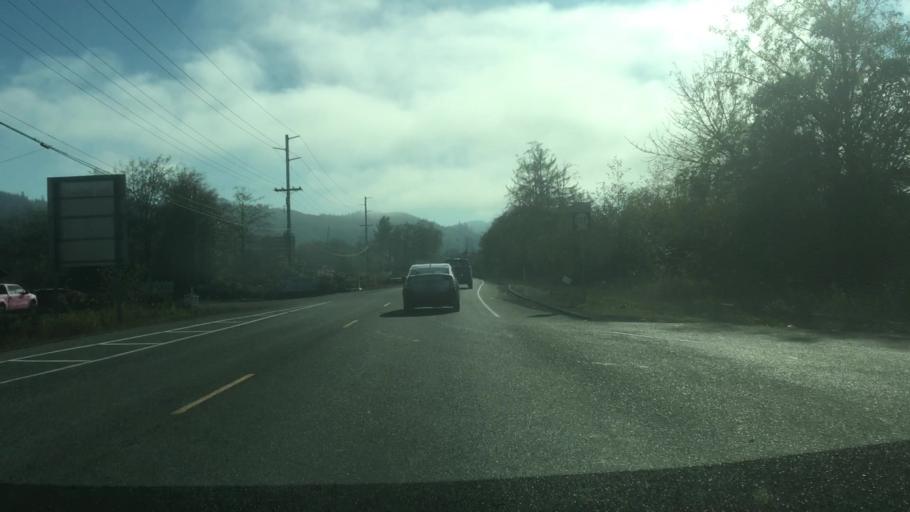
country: US
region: Washington
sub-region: Grays Harbor County
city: Montesano
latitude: 46.9747
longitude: -123.6010
